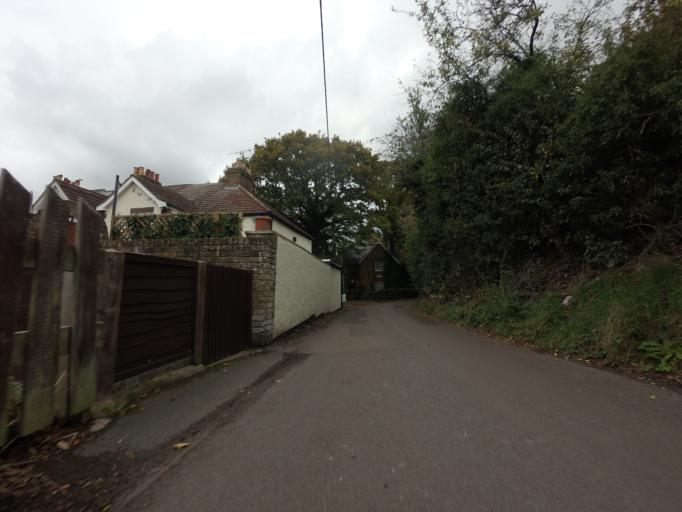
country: GB
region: England
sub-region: Kent
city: Swanley
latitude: 51.3868
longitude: 0.1596
